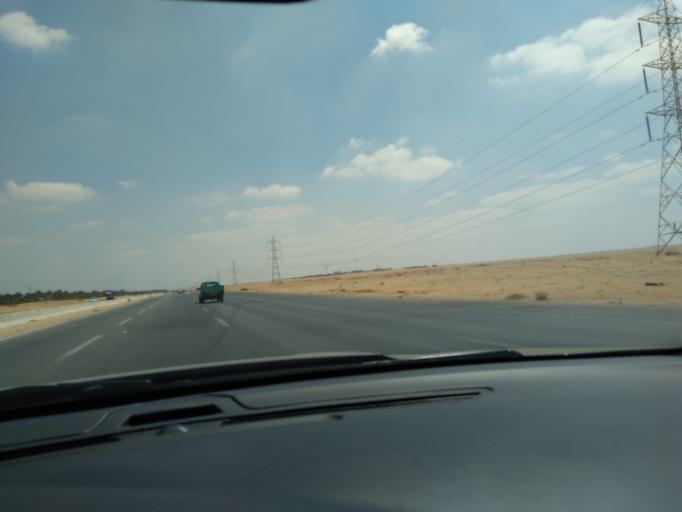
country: EG
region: Al Isma'iliyah
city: At Tall al Kabir
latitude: 30.3831
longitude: 31.9505
